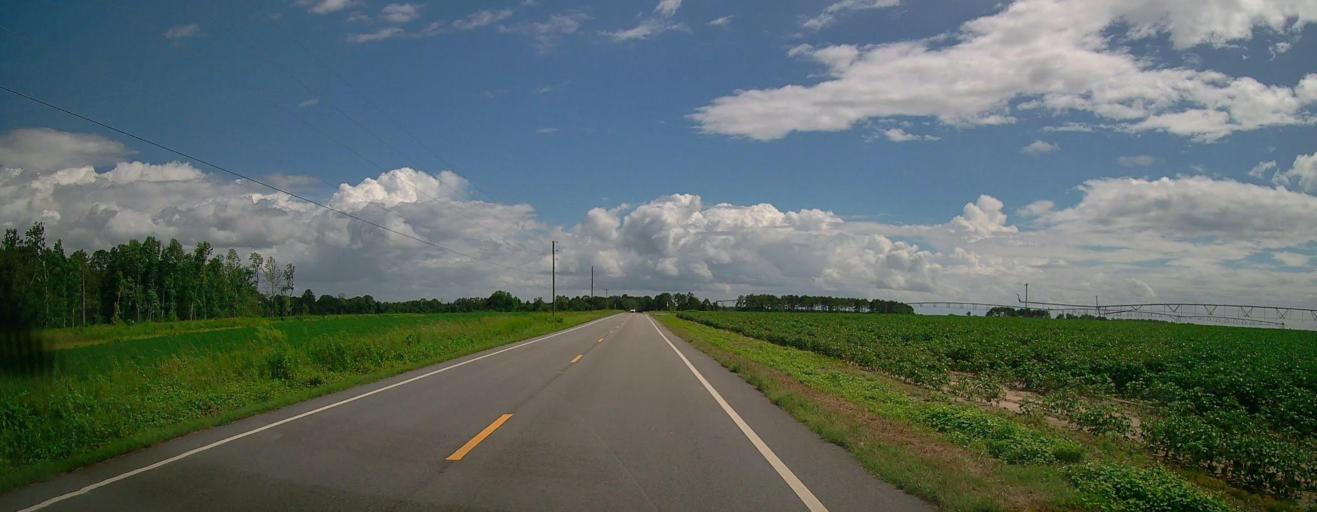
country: US
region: Georgia
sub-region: Irwin County
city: Ocilla
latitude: 31.6503
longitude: -83.1737
